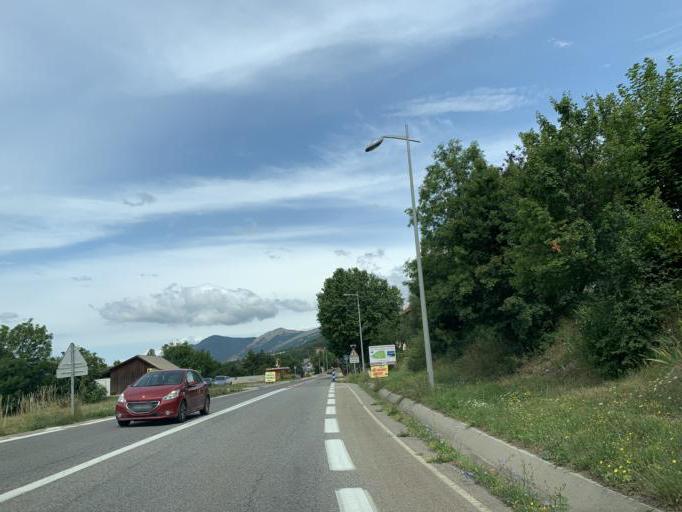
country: FR
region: Provence-Alpes-Cote d'Azur
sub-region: Departement des Hautes-Alpes
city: La Roche-des-Arnauds
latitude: 44.5399
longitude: 6.0167
